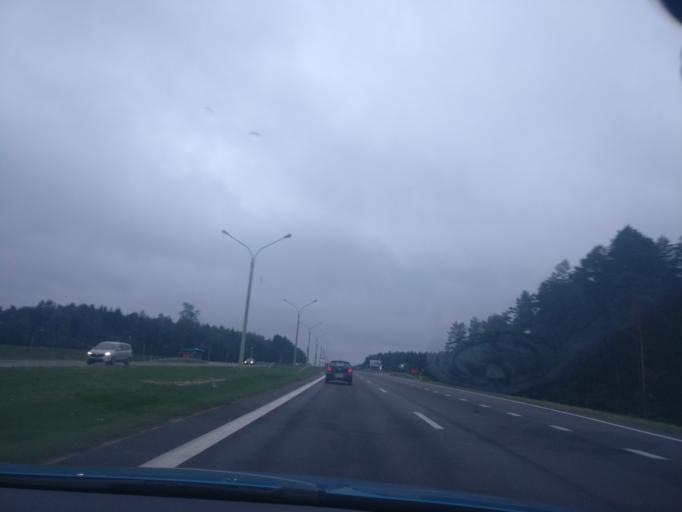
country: BY
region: Minsk
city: Kalodzishchy
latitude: 53.9702
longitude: 27.7519
